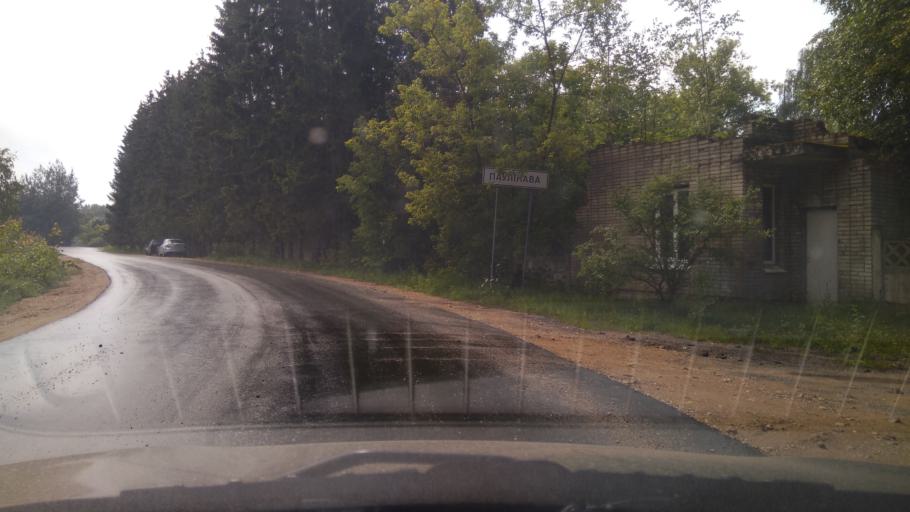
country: BY
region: Brest
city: Baranovichi
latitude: 53.0292
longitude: 25.8186
